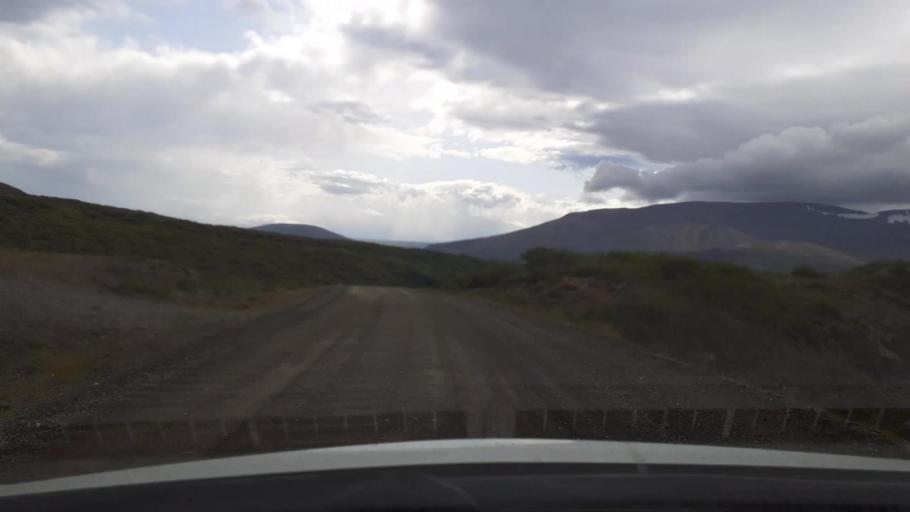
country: IS
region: West
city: Borgarnes
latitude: 64.5586
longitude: -21.6261
